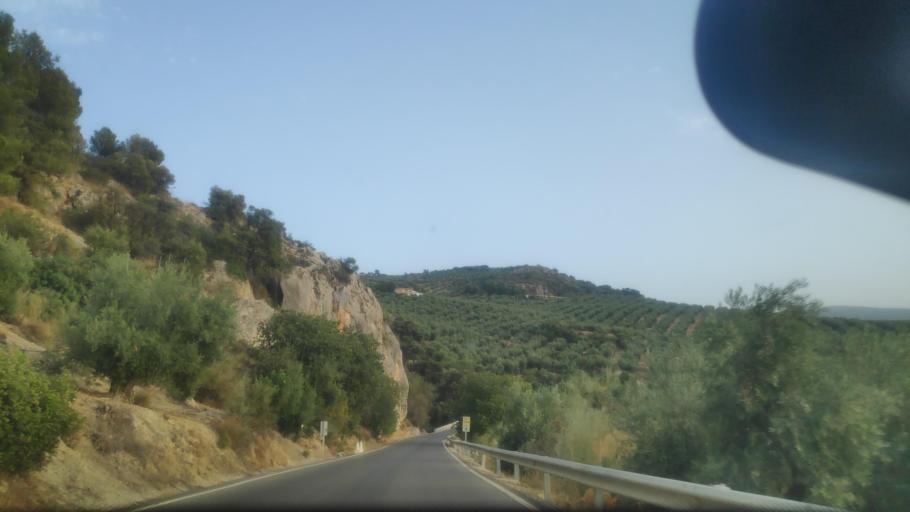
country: ES
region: Andalusia
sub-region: Provincia de Jaen
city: Torres
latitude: 37.8240
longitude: -3.5270
